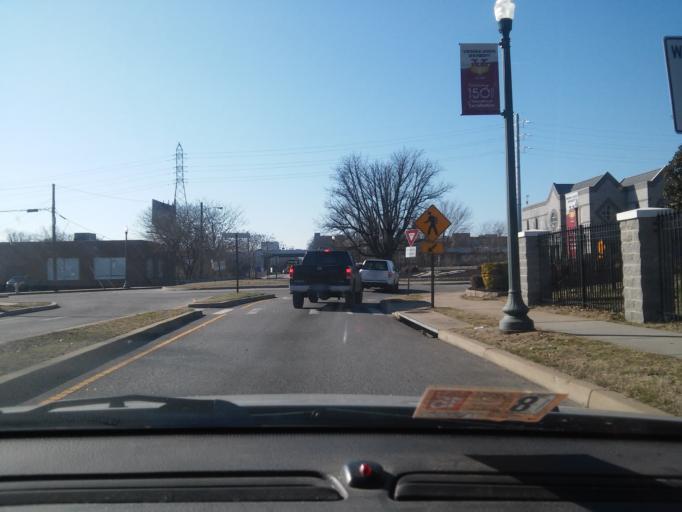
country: US
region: Virginia
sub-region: City of Richmond
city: Richmond
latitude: 37.5601
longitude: -77.4506
